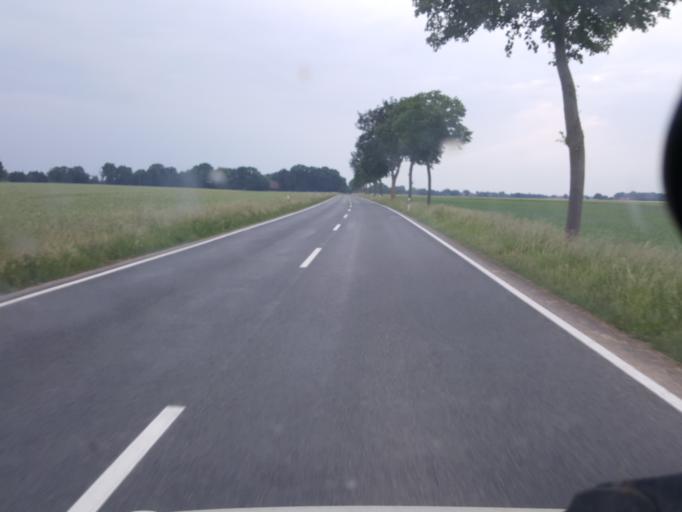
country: DE
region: Lower Saxony
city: Stolzenau
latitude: 52.5000
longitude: 9.0475
